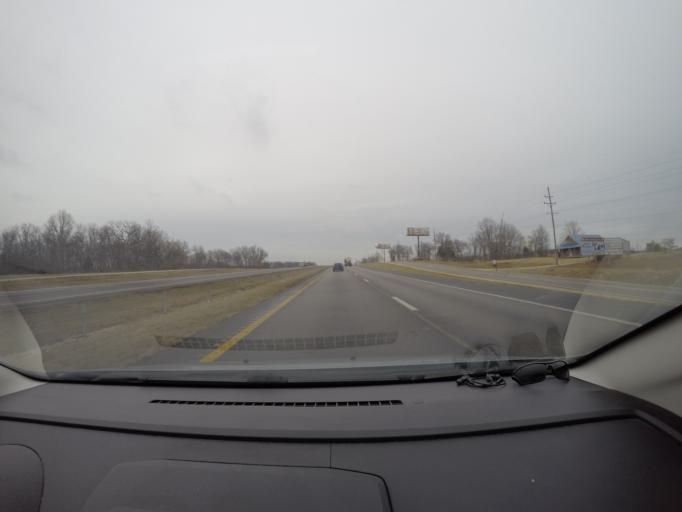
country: US
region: Missouri
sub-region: Warren County
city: Warrenton
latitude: 38.8473
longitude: -91.2749
